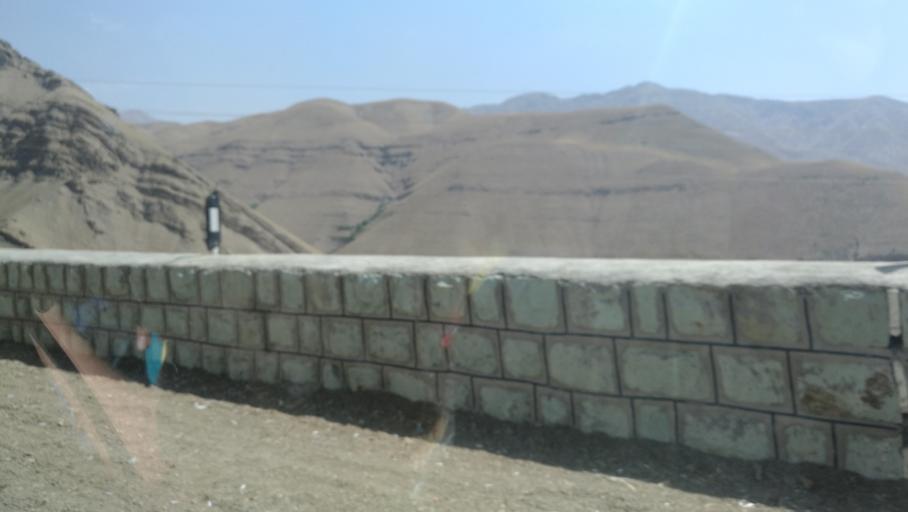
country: IR
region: Alborz
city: Karaj
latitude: 35.9493
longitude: 51.0859
